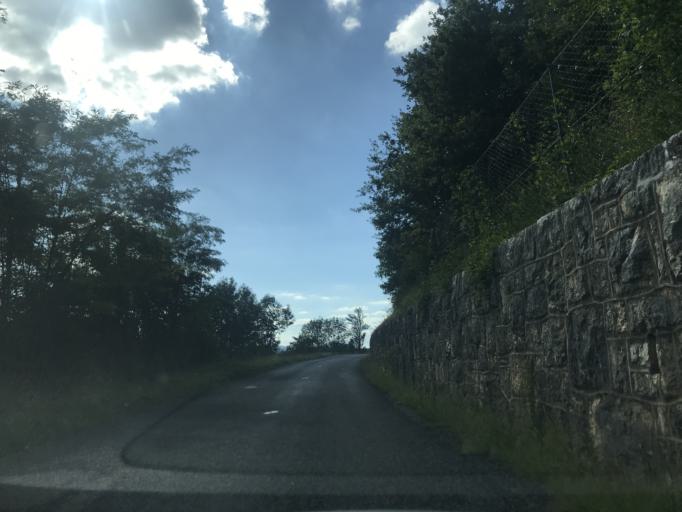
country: FR
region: Rhone-Alpes
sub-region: Departement de la Savoie
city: Yenne
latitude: 45.7153
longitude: 5.8228
